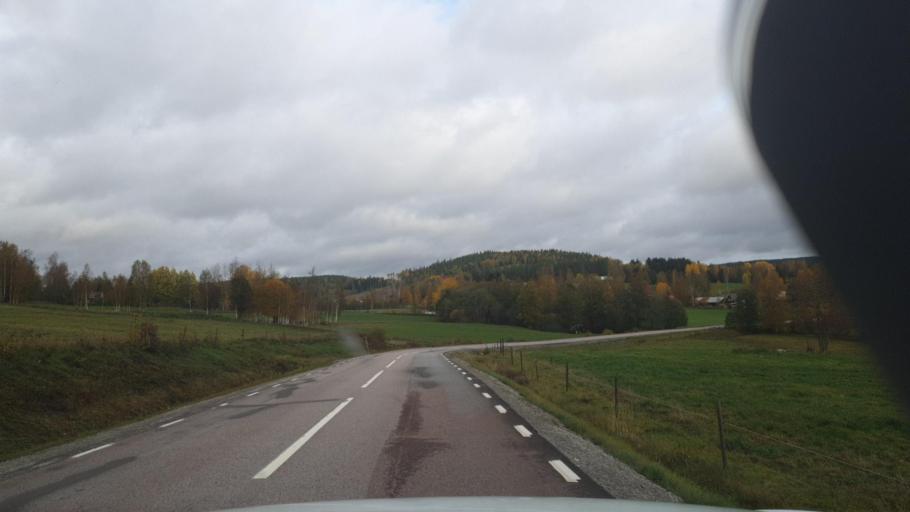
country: SE
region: Vaermland
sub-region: Sunne Kommun
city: Sunne
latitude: 59.6657
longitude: 13.0082
